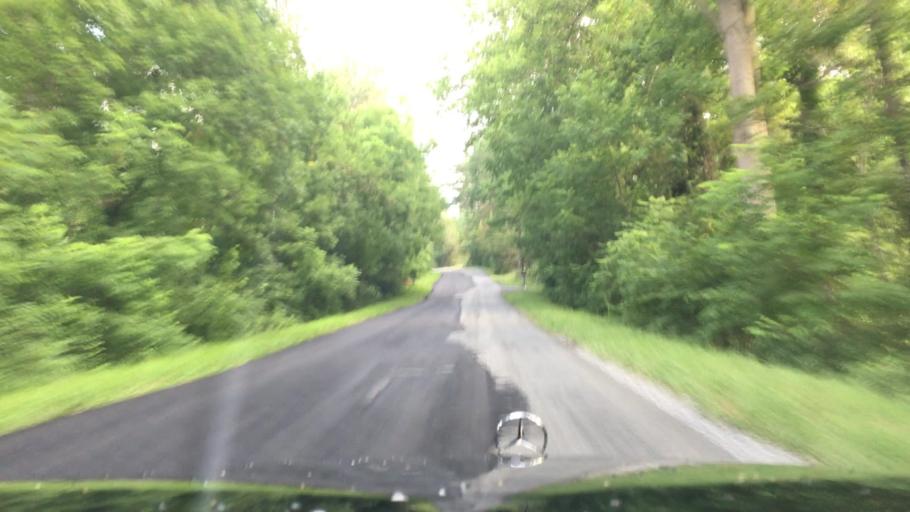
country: US
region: Virginia
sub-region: Campbell County
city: Timberlake
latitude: 37.2483
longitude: -79.3062
